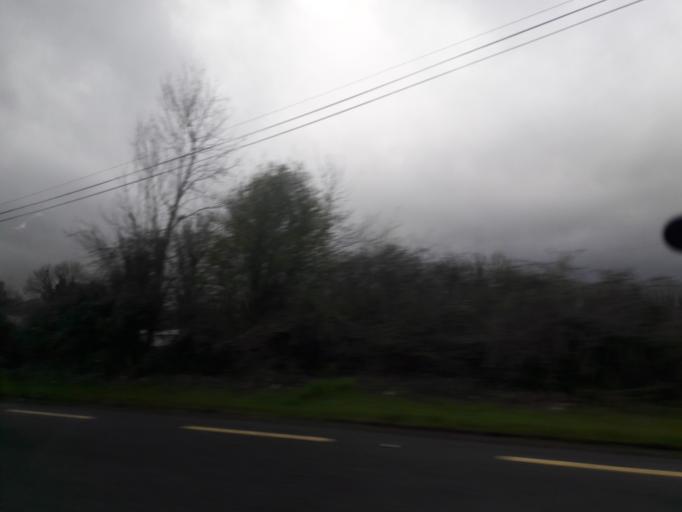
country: IE
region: Leinster
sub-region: An Longfort
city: Longford
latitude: 53.8074
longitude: -7.8852
